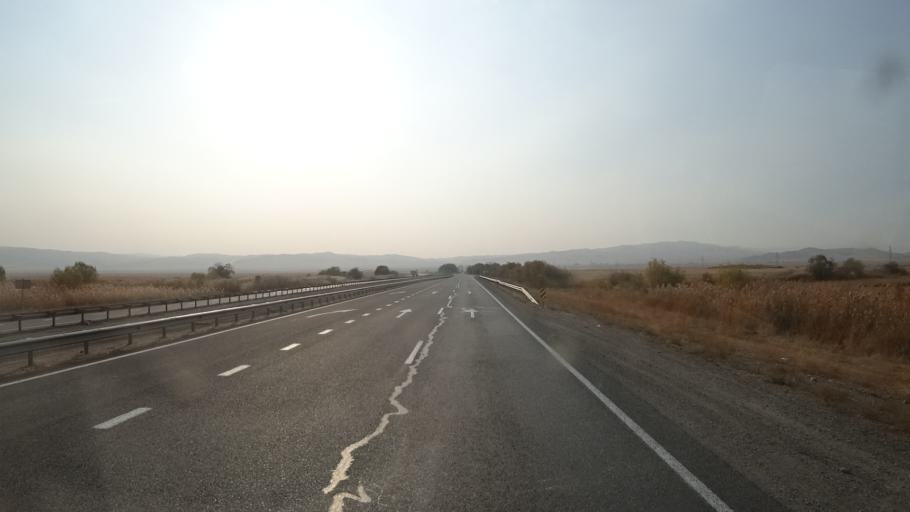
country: KZ
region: Zhambyl
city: Taraz
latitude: 42.7878
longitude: 71.0581
